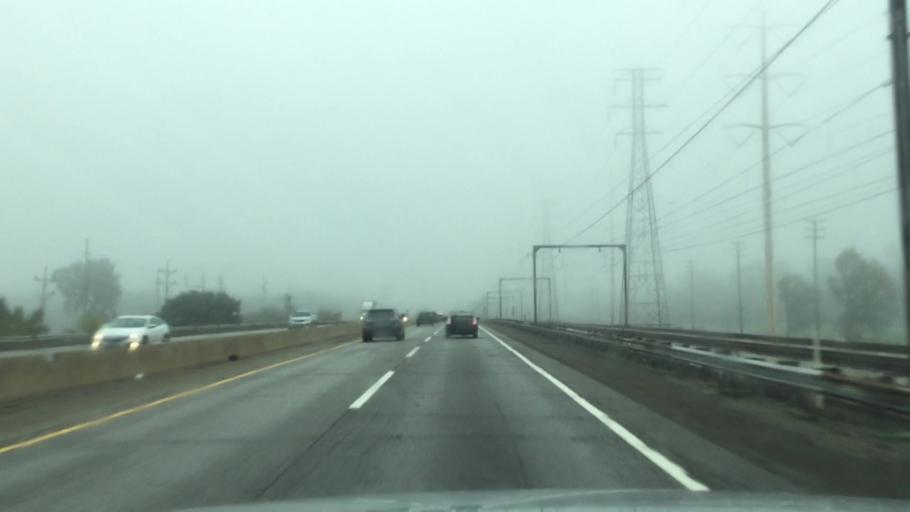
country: US
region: Indiana
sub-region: Lake County
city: East Chicago
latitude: 41.6106
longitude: -87.4609
